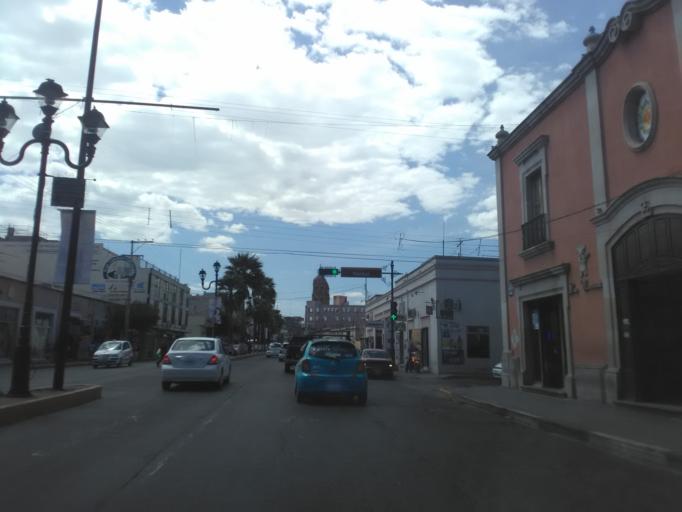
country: MX
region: Durango
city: Victoria de Durango
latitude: 24.0252
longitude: -104.6674
